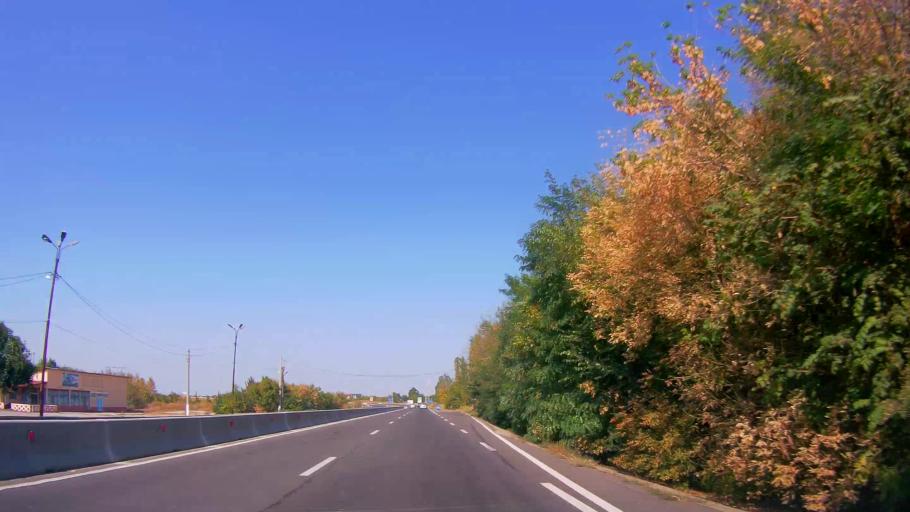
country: RO
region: Giurgiu
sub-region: Comuna Adunatii-Copaceni
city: Adunatii-Copaceni
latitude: 44.2352
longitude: 26.0356
